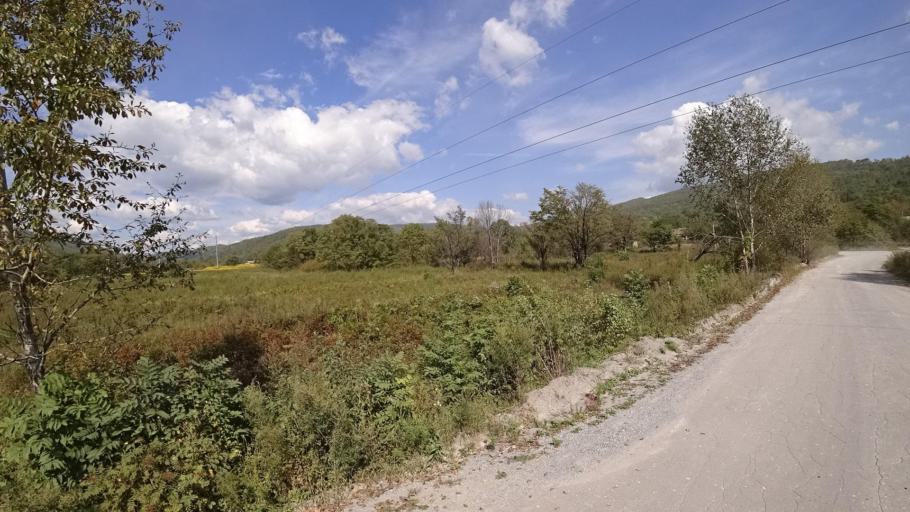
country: RU
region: Jewish Autonomous Oblast
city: Londoko
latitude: 49.0221
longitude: 131.9305
